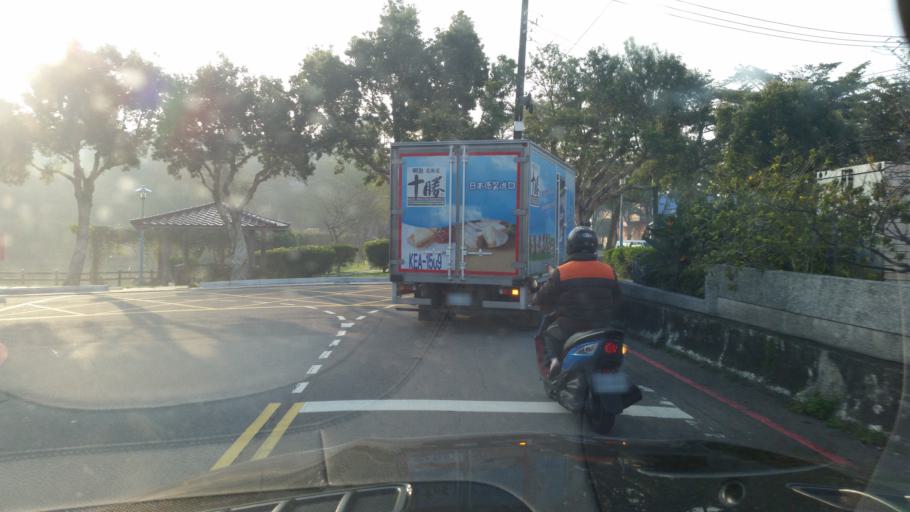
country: TW
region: Taiwan
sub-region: Taoyuan
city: Taoyuan
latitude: 25.0575
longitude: 121.3569
